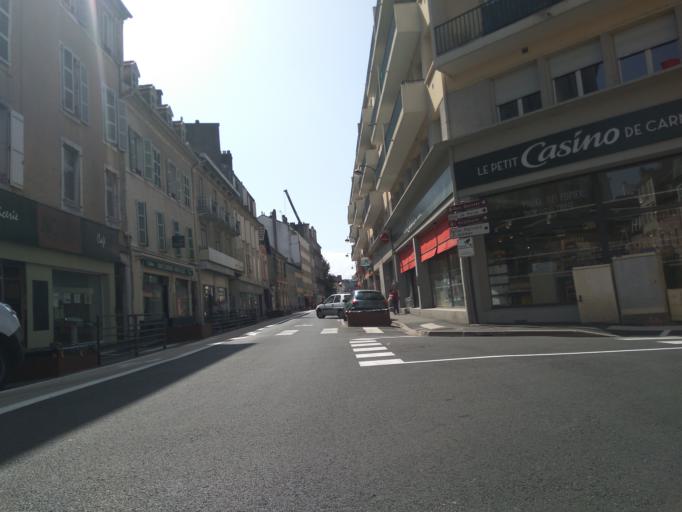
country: FR
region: Aquitaine
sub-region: Departement des Pyrenees-Atlantiques
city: Pau
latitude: 43.3015
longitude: -0.3693
